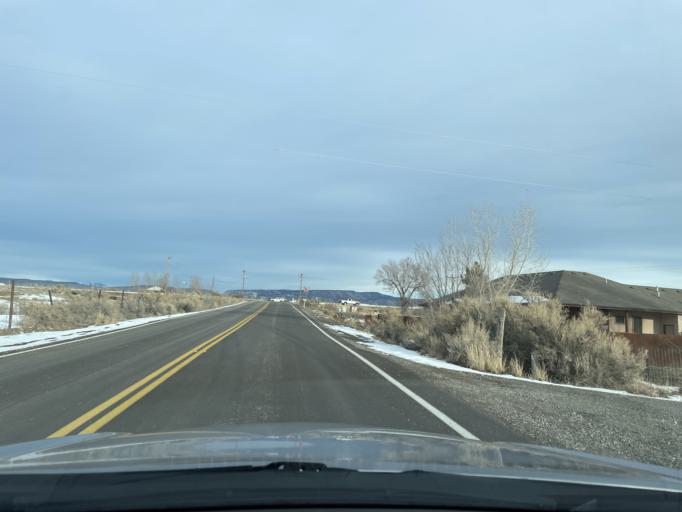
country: US
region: Colorado
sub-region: Montrose County
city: Olathe
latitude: 38.6495
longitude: -107.9917
